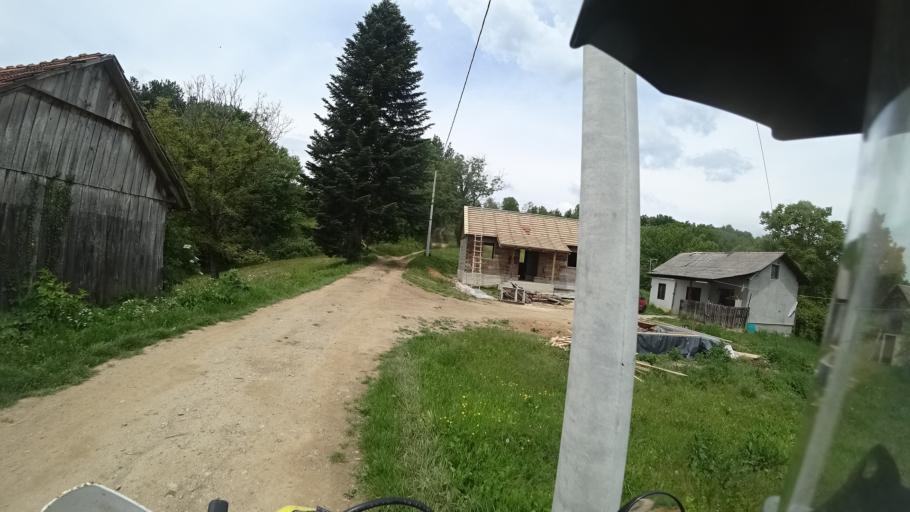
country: HR
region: Karlovacka
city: Vojnic
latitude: 45.2454
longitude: 15.6508
